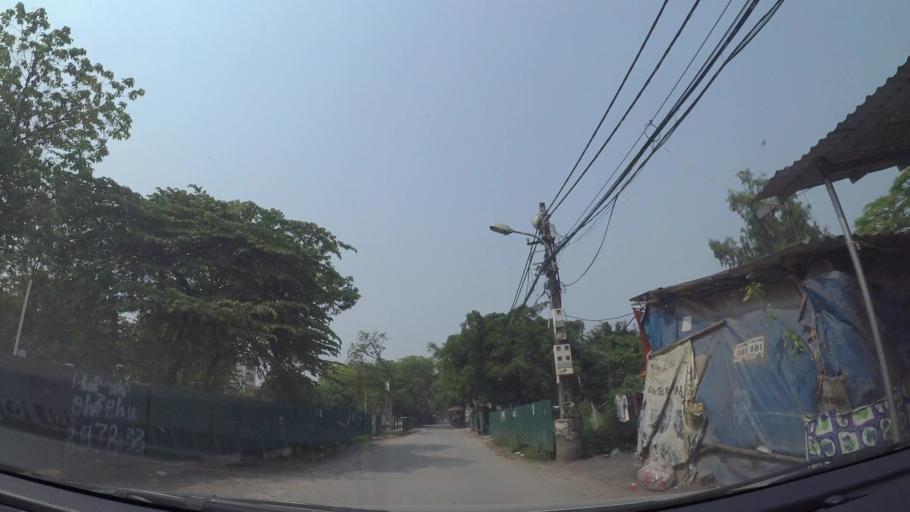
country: VN
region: Ha Noi
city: Ha Dong
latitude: 20.9965
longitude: 105.7562
